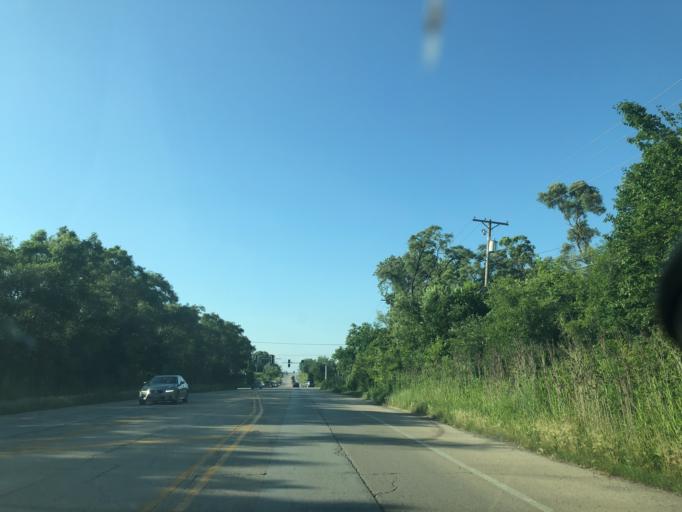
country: US
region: Illinois
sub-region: Cook County
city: Orland Hills
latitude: 41.5849
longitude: -87.8909
